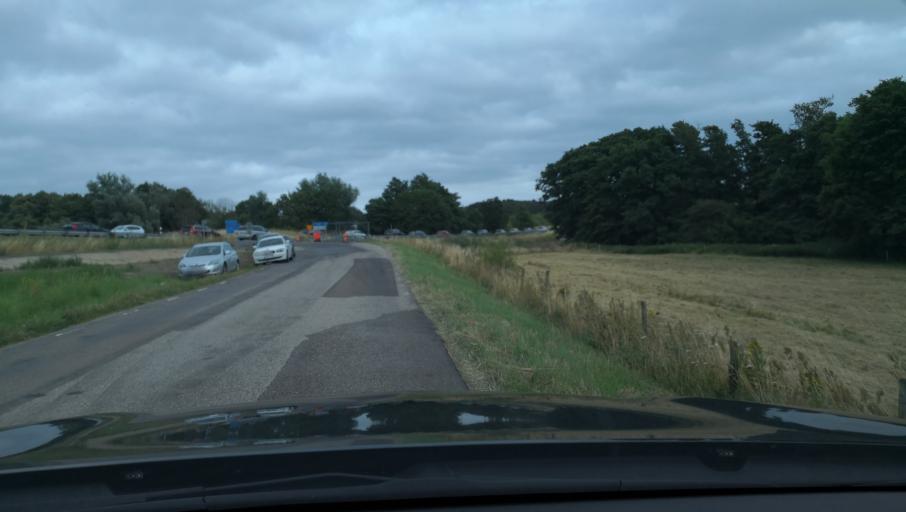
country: SE
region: Skane
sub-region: Simrishamns Kommun
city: Kivik
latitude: 55.6992
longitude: 14.1945
